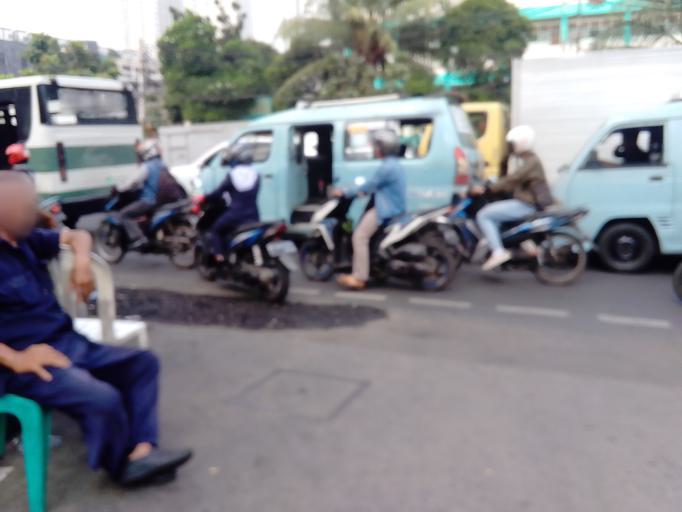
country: ID
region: Jakarta Raya
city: Jakarta
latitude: -6.1971
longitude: 106.8141
